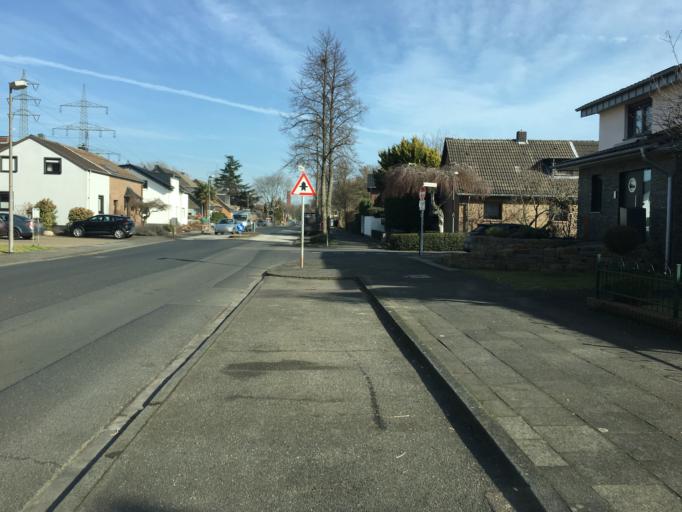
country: DE
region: North Rhine-Westphalia
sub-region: Regierungsbezirk Koln
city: Mengenich
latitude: 51.0116
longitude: 6.8976
